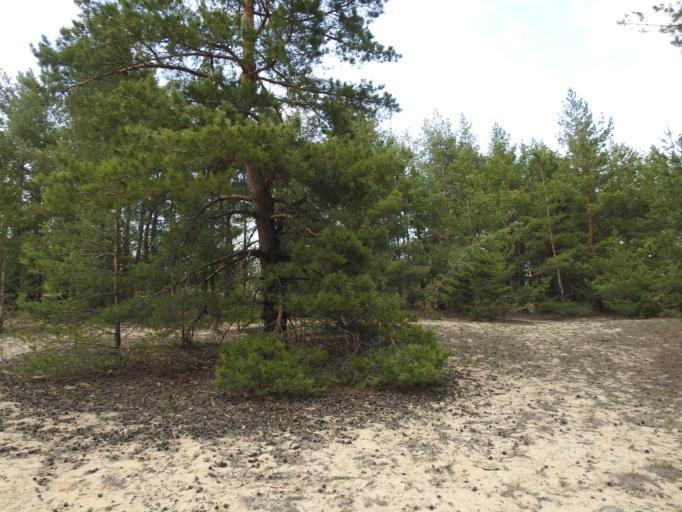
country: RU
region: Saratov
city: Krasnyy Oktyabr'
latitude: 51.4268
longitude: 45.5428
